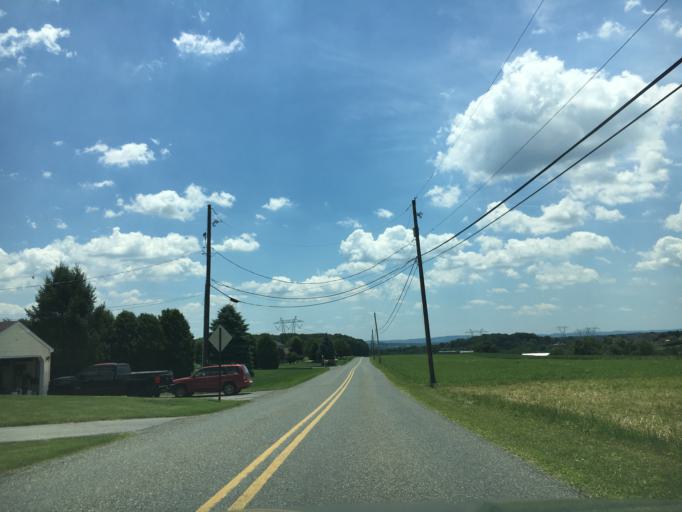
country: US
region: Pennsylvania
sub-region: Lehigh County
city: Schnecksville
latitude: 40.6807
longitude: -75.5816
